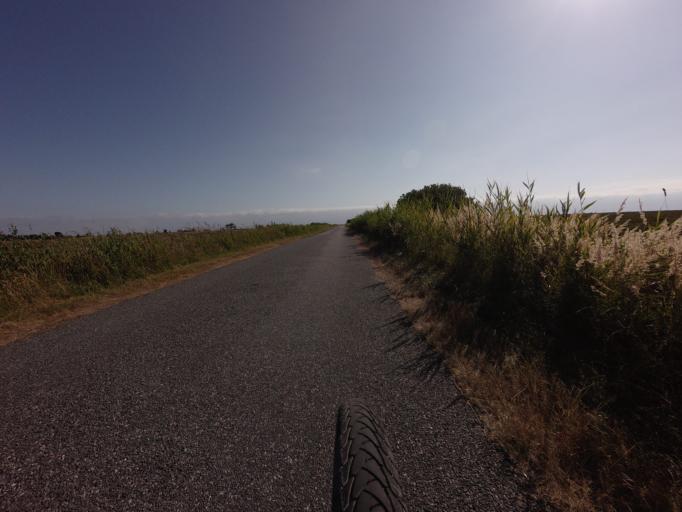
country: DK
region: North Denmark
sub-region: Laeso Kommune
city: Byrum
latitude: 57.2562
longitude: 10.8835
